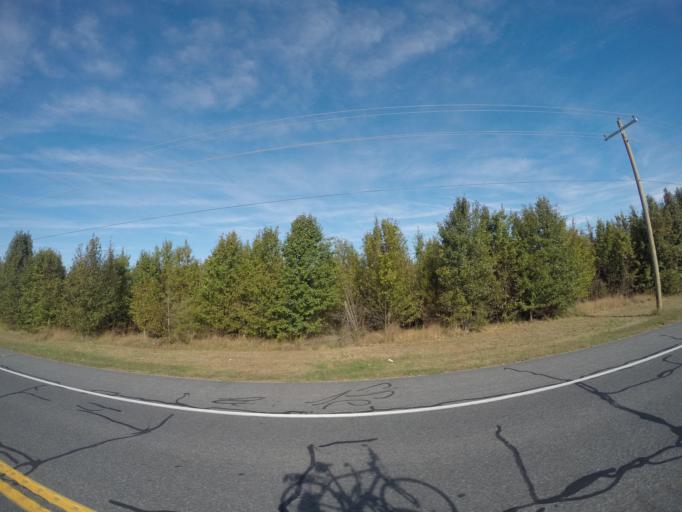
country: US
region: Delaware
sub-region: Sussex County
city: Bridgeville
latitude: 38.8026
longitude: -75.5425
